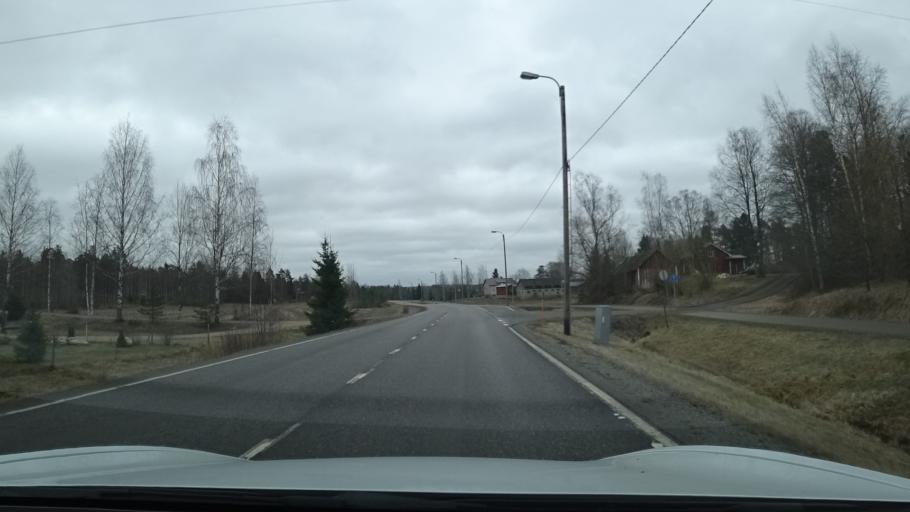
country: FI
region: Uusimaa
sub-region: Porvoo
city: Askola
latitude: 60.4960
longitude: 25.5125
